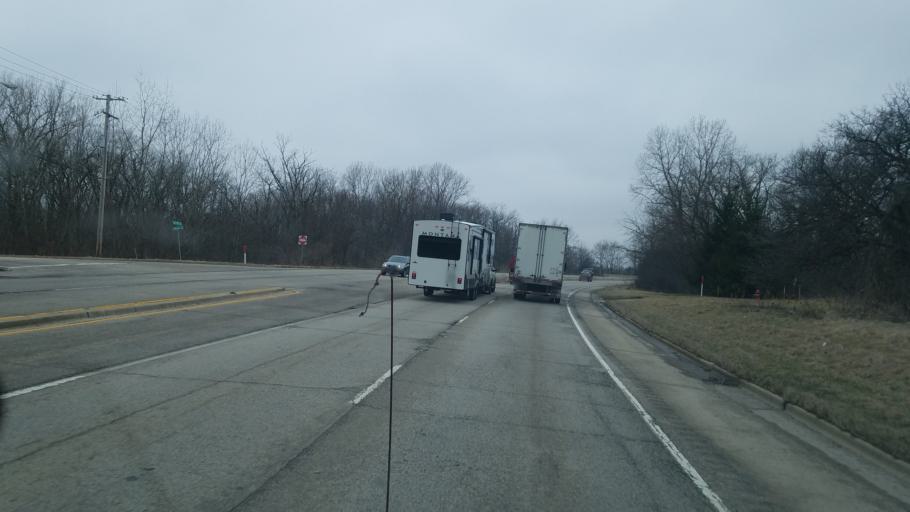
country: US
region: Illinois
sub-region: Lake County
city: Gurnee
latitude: 42.3792
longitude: -87.9138
